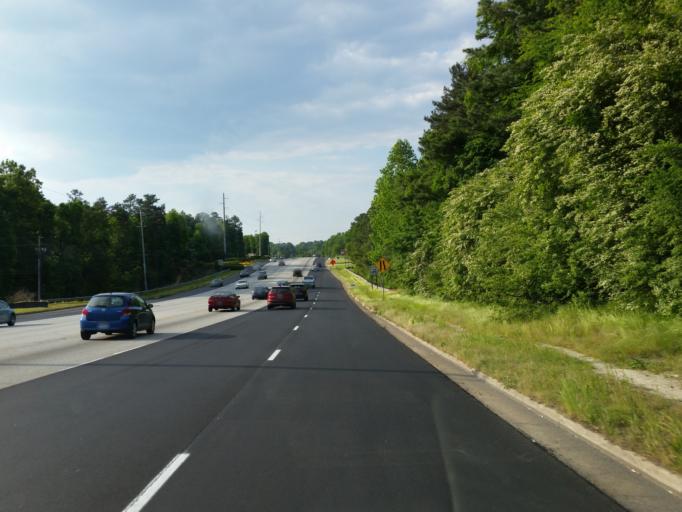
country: US
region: Georgia
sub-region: Cobb County
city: Vinings
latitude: 33.8312
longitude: -84.4926
